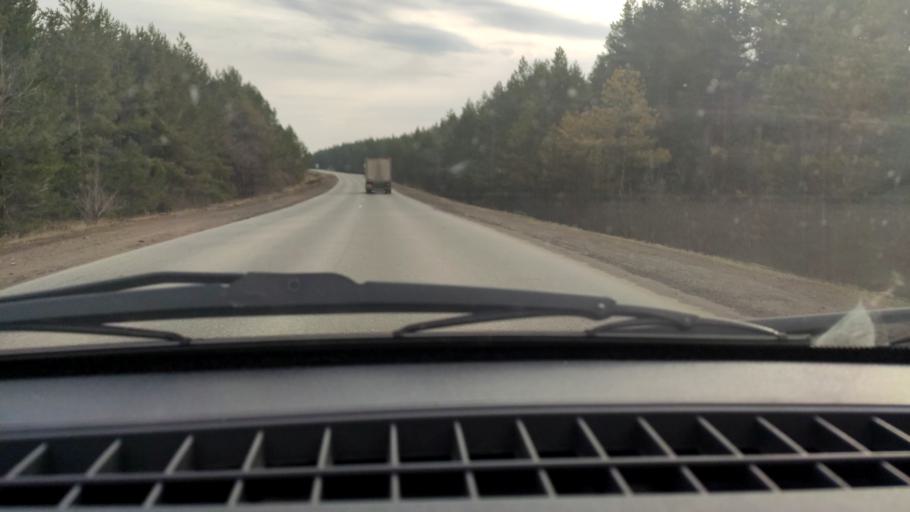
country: RU
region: Bashkortostan
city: Davlekanovo
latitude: 54.2424
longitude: 55.0683
